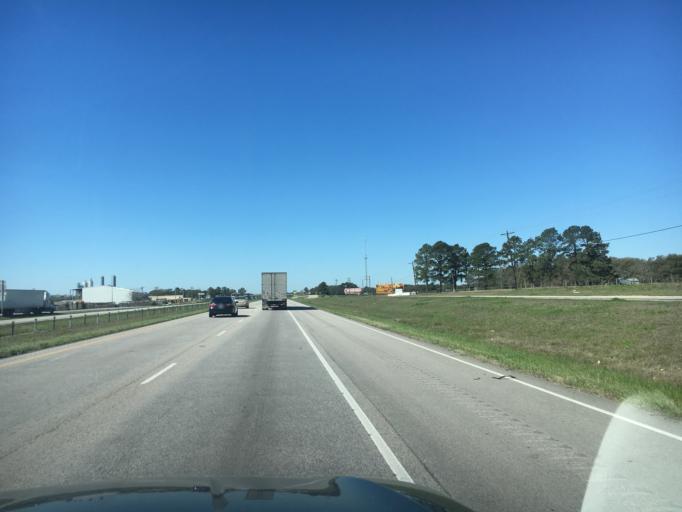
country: US
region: Texas
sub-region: Colorado County
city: Columbus
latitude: 29.7261
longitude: -96.4069
